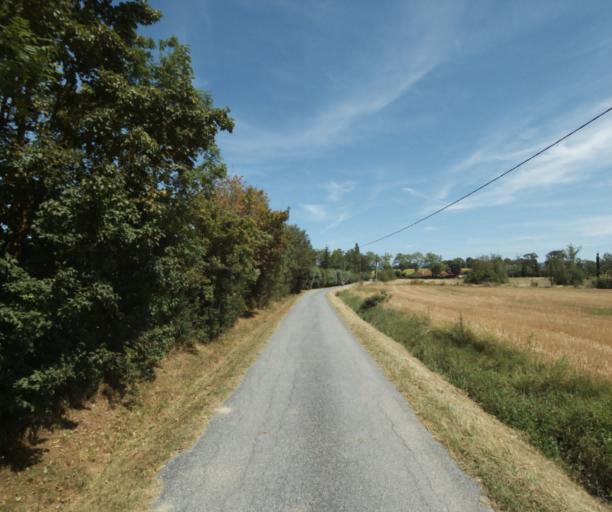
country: FR
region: Midi-Pyrenees
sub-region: Departement de la Haute-Garonne
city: Revel
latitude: 43.5061
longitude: 2.0088
